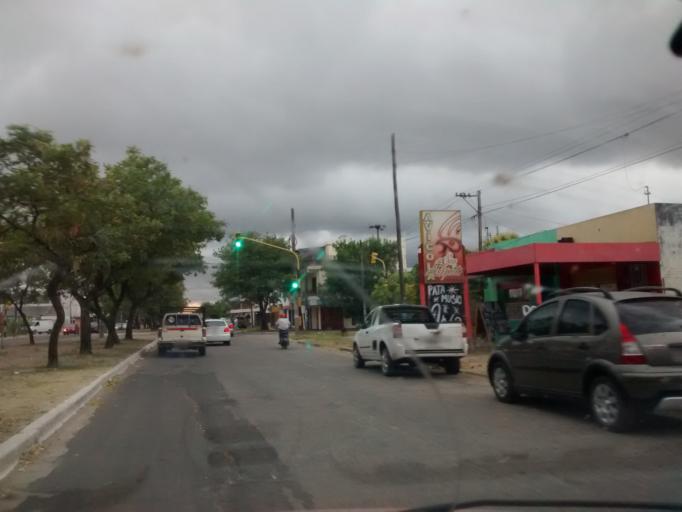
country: AR
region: Chaco
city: Resistencia
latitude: -27.4485
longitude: -59.0122
